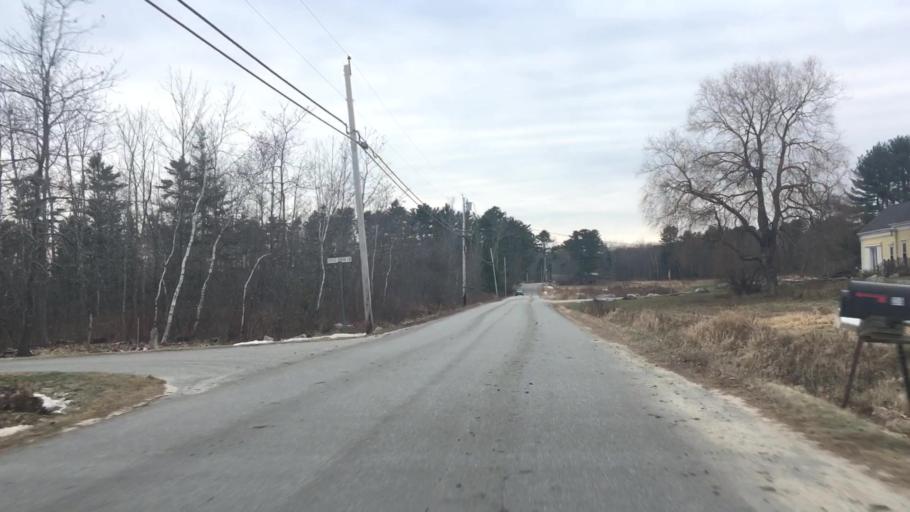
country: US
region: Maine
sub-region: Cumberland County
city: Freeport
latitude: 43.8343
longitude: -70.0786
